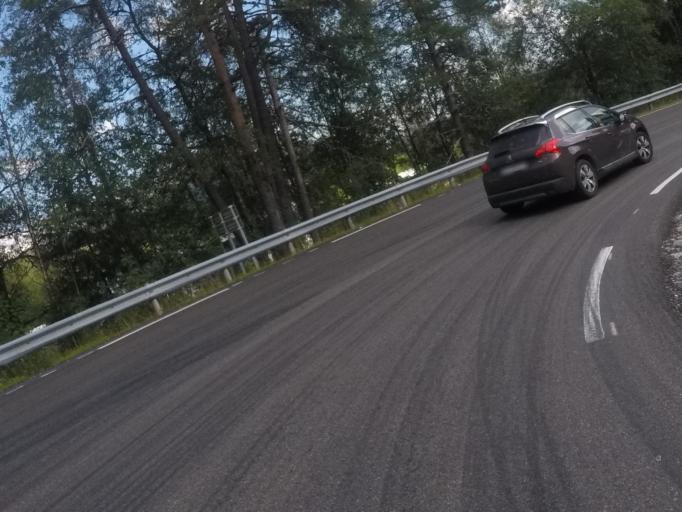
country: NO
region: Sogn og Fjordane
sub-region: Forde
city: Forde
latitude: 61.4457
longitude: 5.8183
